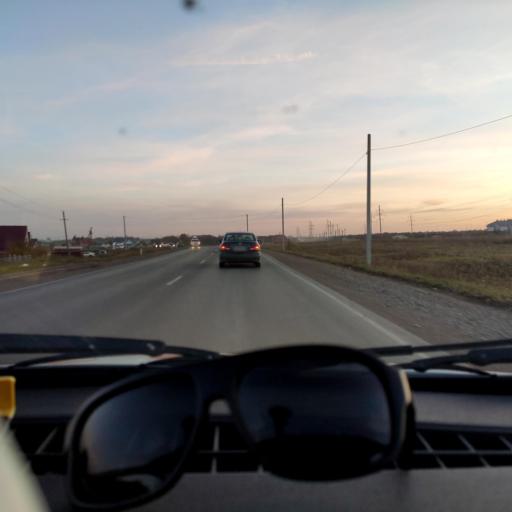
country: RU
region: Bashkortostan
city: Avdon
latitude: 54.7452
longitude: 55.7957
